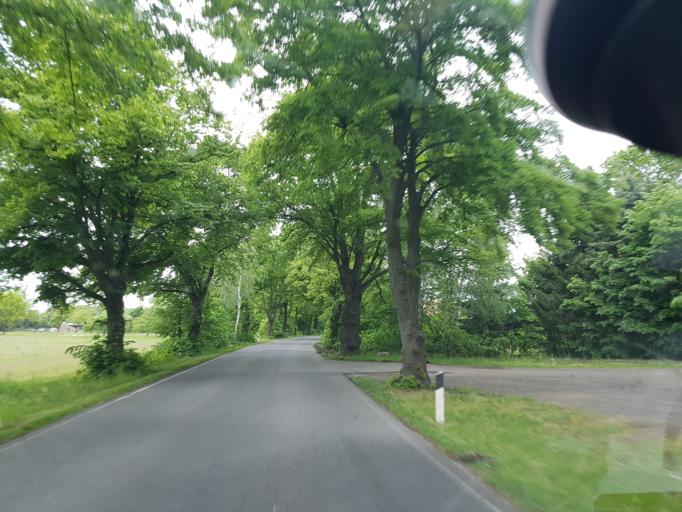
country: DE
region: Brandenburg
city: Drebkau
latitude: 51.6354
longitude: 14.2576
